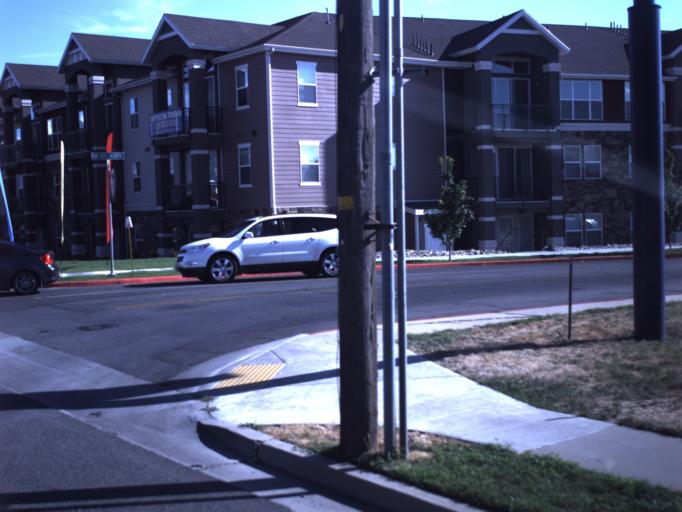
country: US
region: Utah
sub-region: Utah County
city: Orem
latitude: 40.3146
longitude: -111.7028
